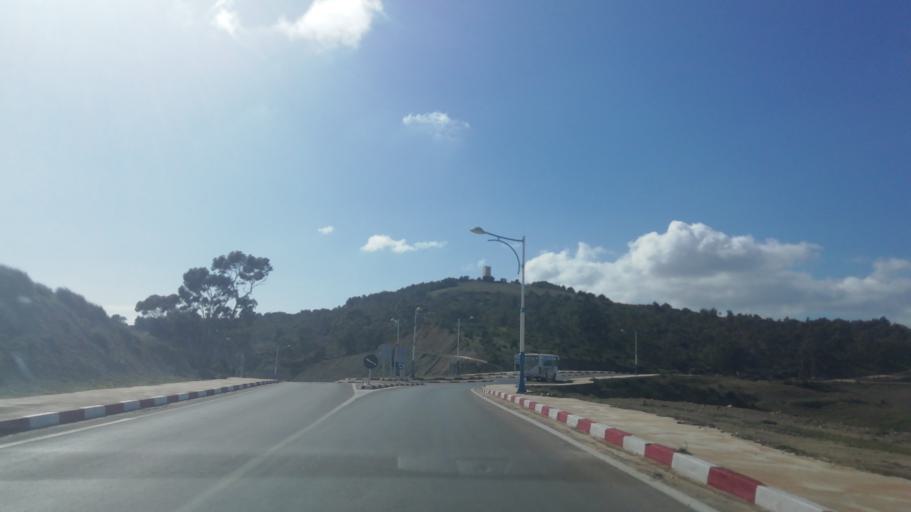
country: DZ
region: Relizane
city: Djidiouia
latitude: 36.0966
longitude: 0.5221
